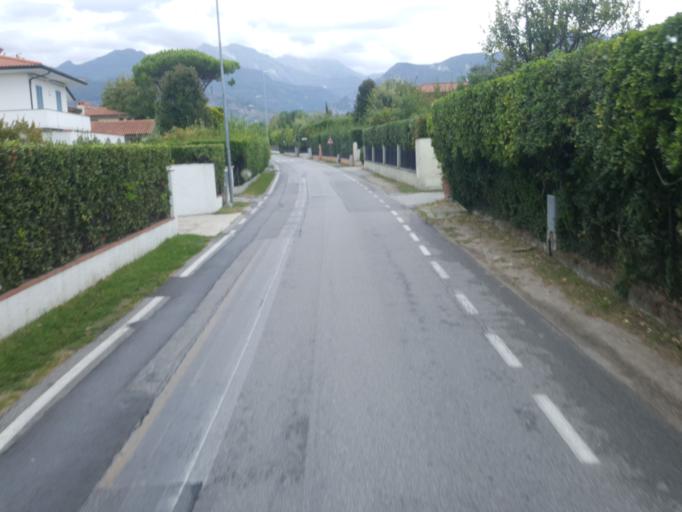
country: IT
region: Tuscany
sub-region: Provincia di Lucca
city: Forte dei Marmi
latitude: 43.9681
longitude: 10.1781
